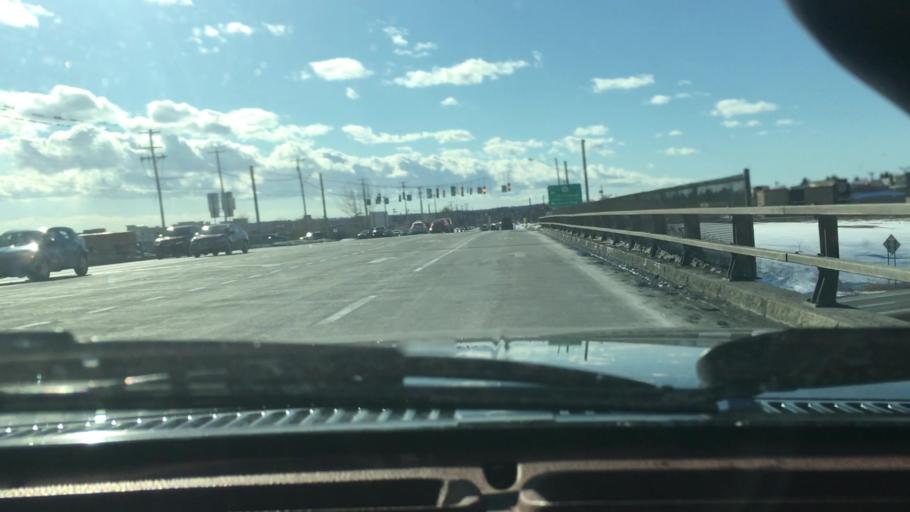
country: US
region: New York
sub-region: Onondaga County
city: Liverpool
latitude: 43.1856
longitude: -76.2313
